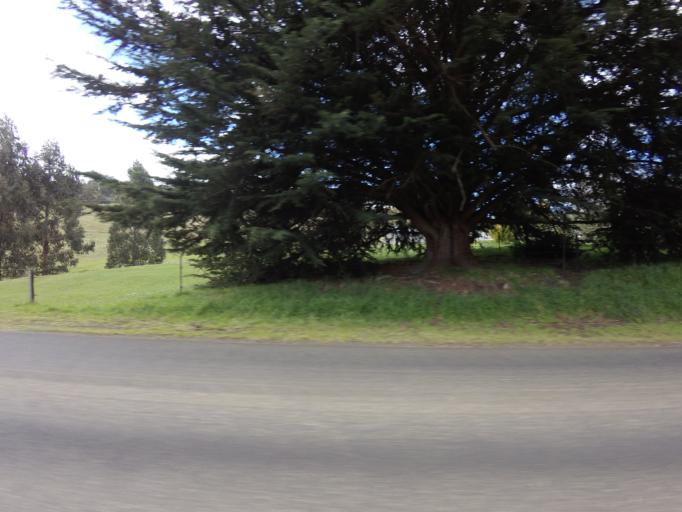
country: AU
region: Tasmania
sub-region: Huon Valley
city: Geeveston
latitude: -43.1912
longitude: 146.9373
